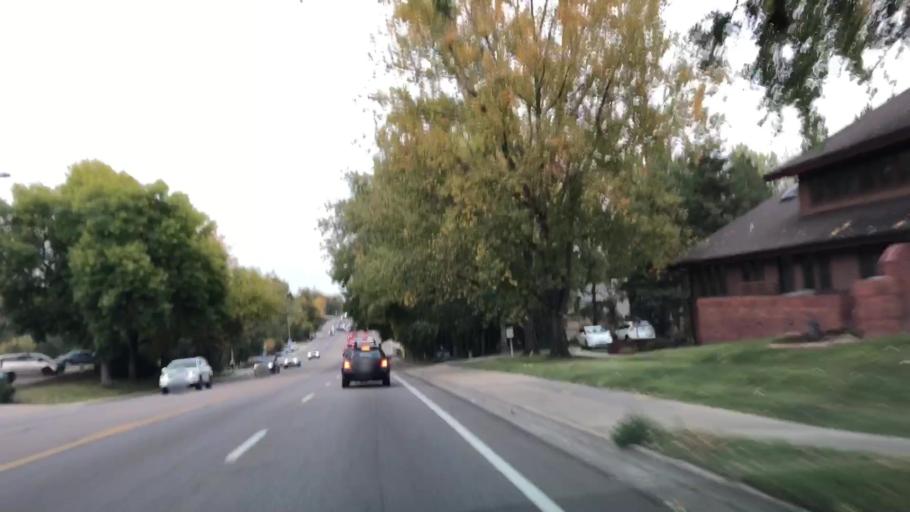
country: US
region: Colorado
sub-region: Larimer County
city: Fort Collins
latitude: 40.5640
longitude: -105.0579
